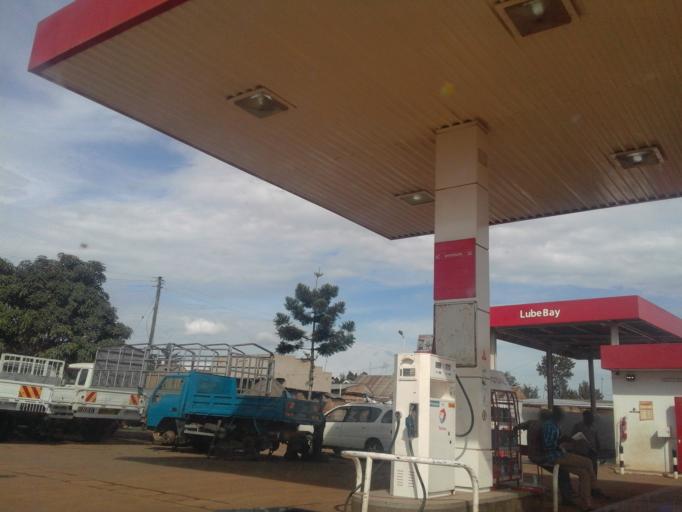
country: UG
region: Central Region
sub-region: Lwengo District
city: Lwengo
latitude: -0.3530
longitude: 31.5535
